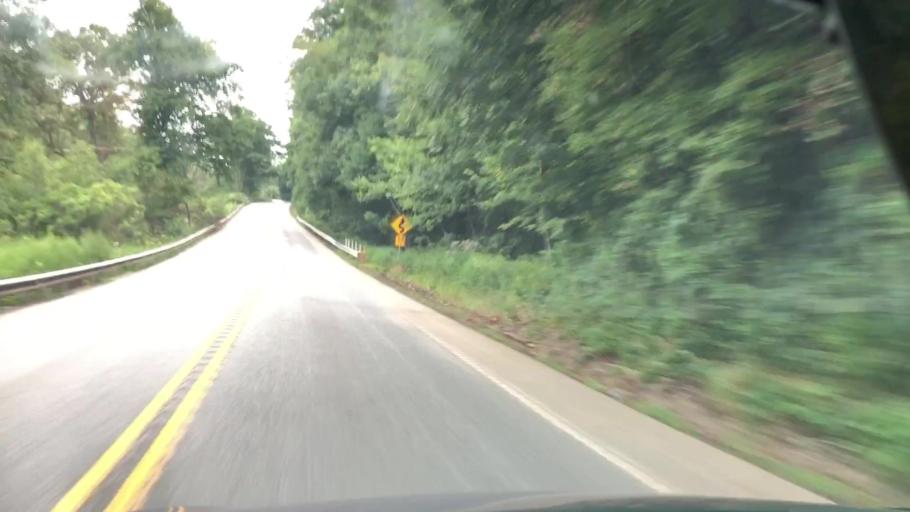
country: US
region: Pennsylvania
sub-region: Venango County
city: Hasson Heights
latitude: 41.5005
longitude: -79.7017
